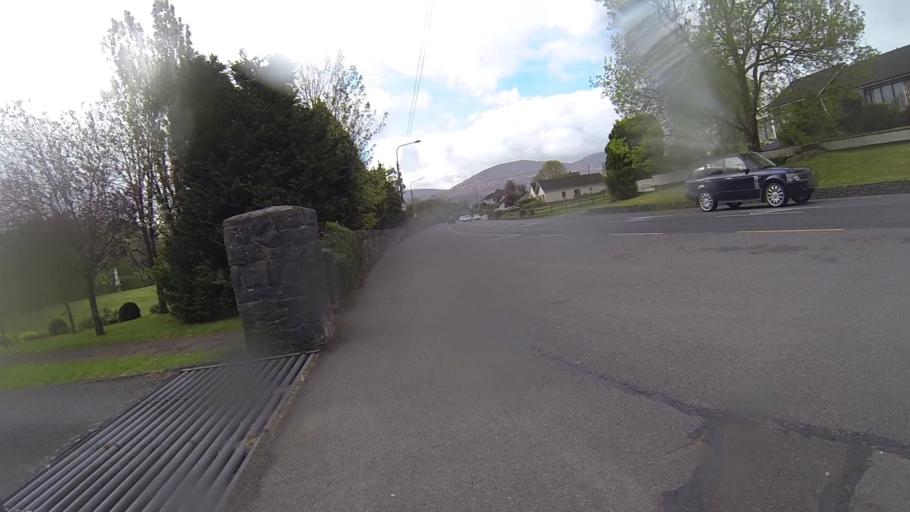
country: IE
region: Munster
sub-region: Ciarrai
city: Kenmare
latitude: 51.8835
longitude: -9.5859
